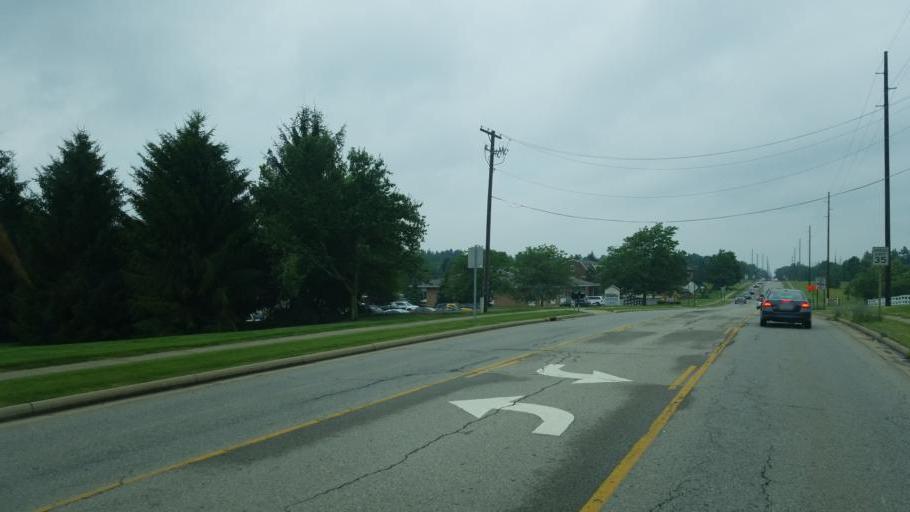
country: US
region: Ohio
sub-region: Richland County
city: Mansfield
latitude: 40.7420
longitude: -82.5517
